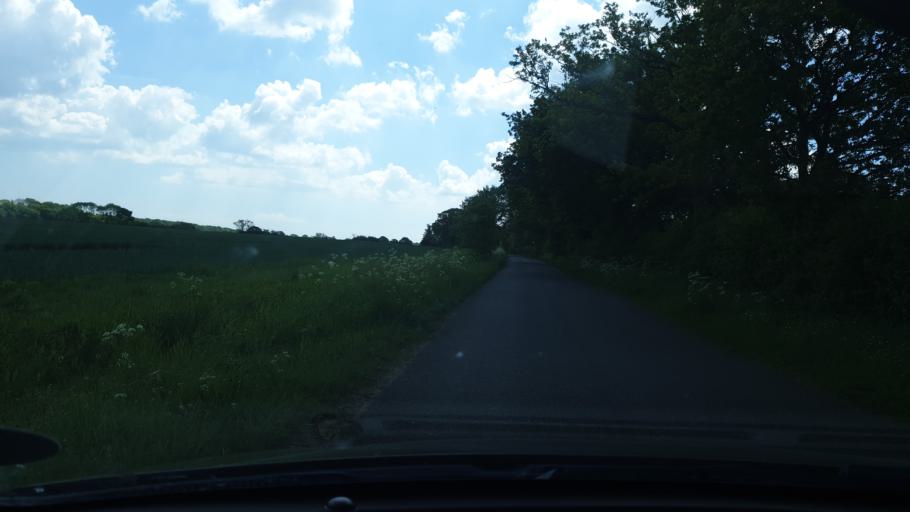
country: GB
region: England
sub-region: Essex
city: Great Bentley
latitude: 51.8485
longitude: 1.0882
